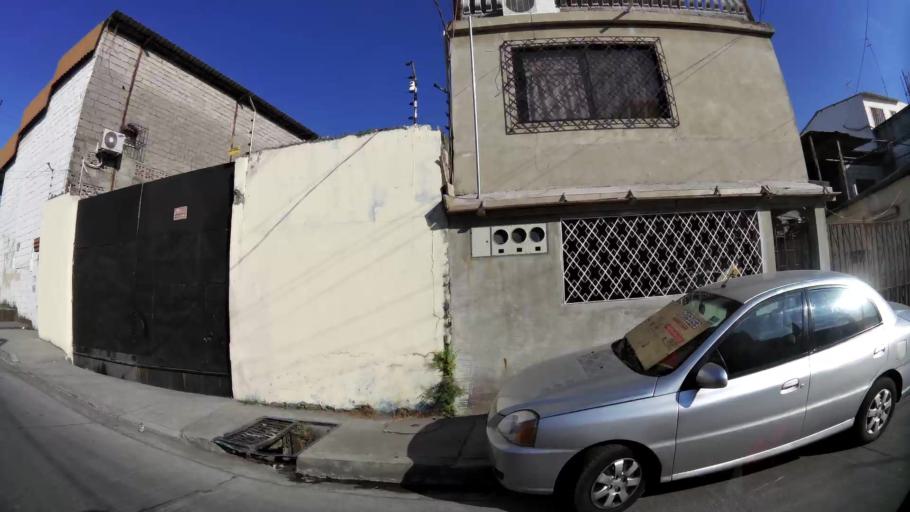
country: EC
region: Guayas
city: Guayaquil
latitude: -2.1568
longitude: -79.9134
